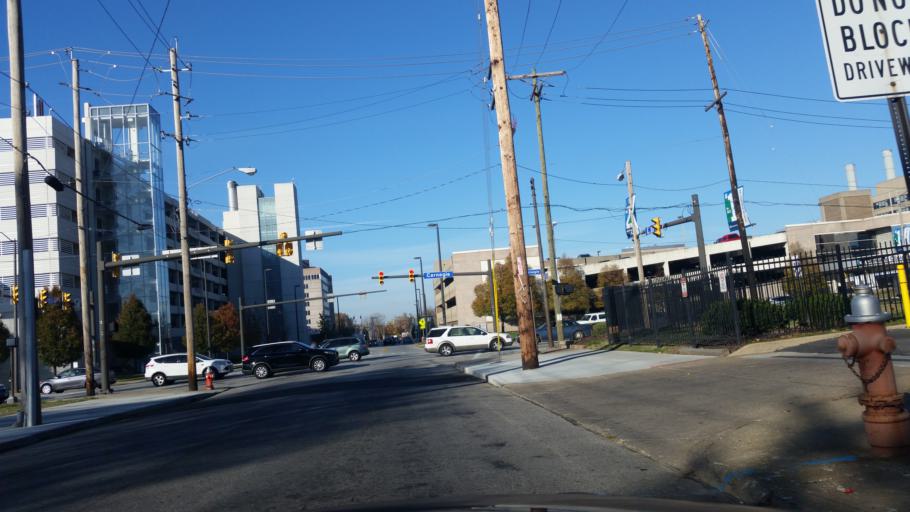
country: US
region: Ohio
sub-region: Cuyahoga County
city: Bratenahl
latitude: 41.5006
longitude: -81.6245
